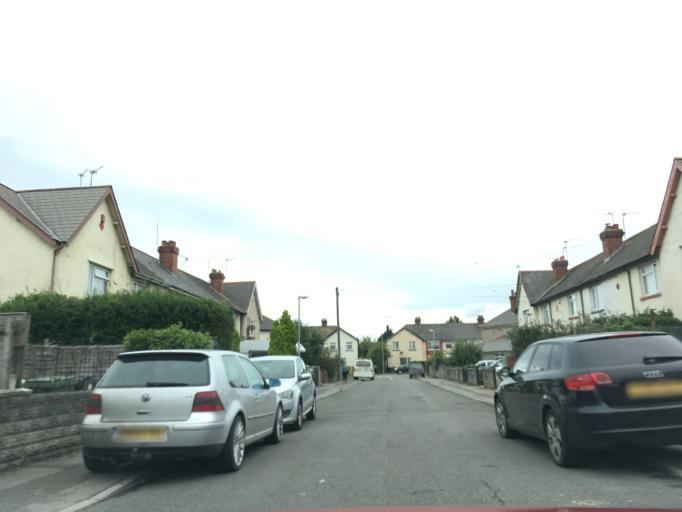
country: GB
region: Wales
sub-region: Cardiff
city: Cardiff
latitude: 51.4835
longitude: -3.1415
